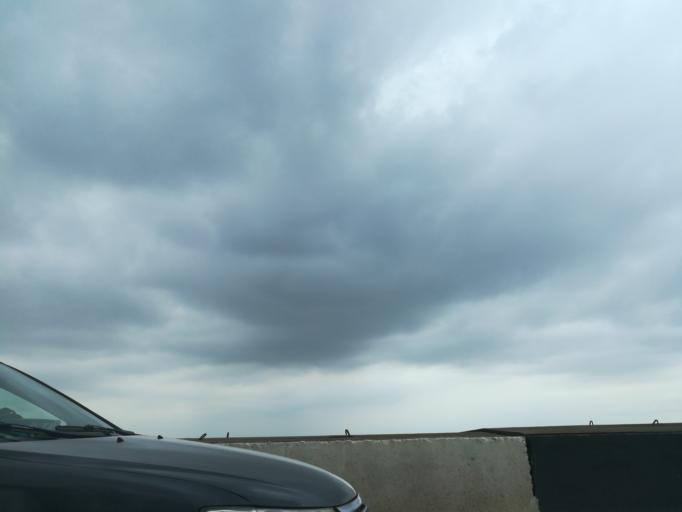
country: NG
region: Lagos
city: Makoko
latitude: 6.5195
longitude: 3.4052
